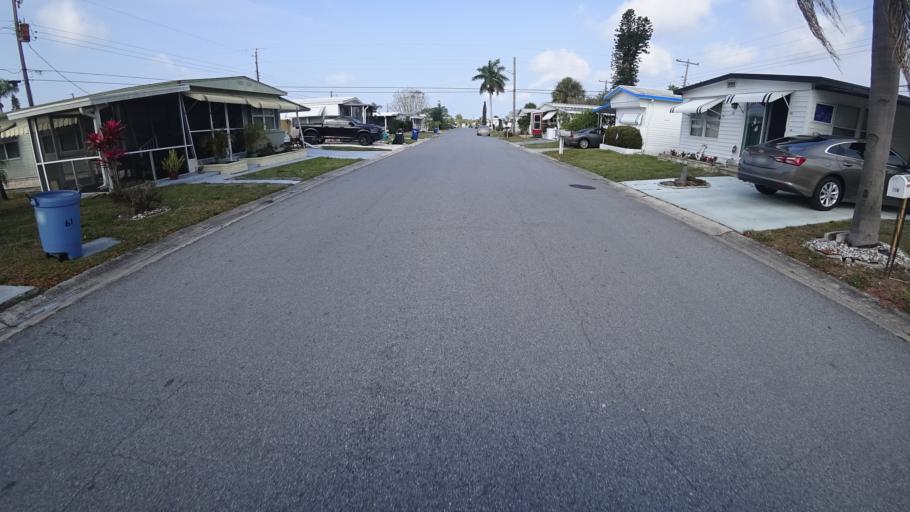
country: US
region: Florida
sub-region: Manatee County
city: South Bradenton
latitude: 27.4548
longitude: -82.5686
